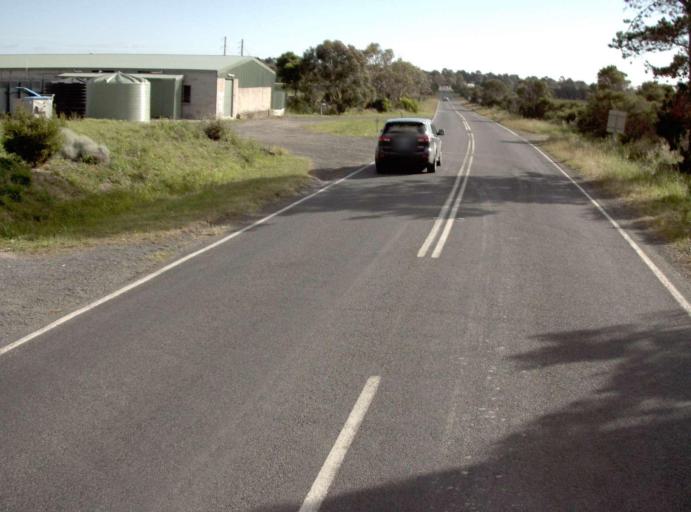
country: AU
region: Victoria
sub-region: Bass Coast
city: North Wonthaggi
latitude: -38.6182
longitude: 145.7389
